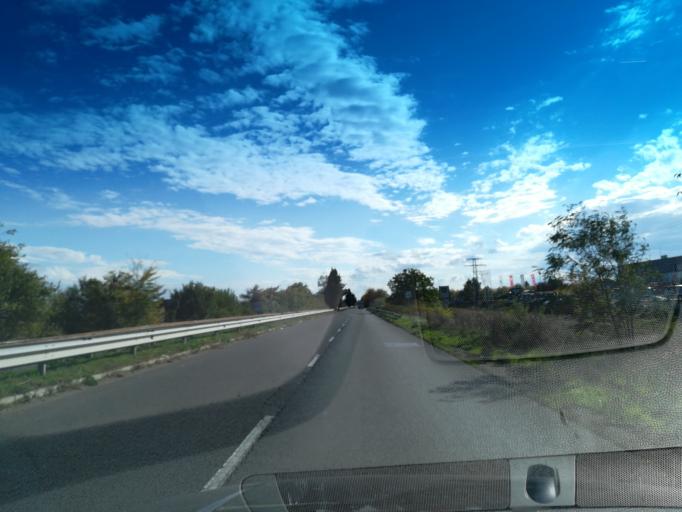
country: BG
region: Stara Zagora
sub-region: Obshtina Stara Zagora
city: Stara Zagora
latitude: 42.3910
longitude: 25.6469
